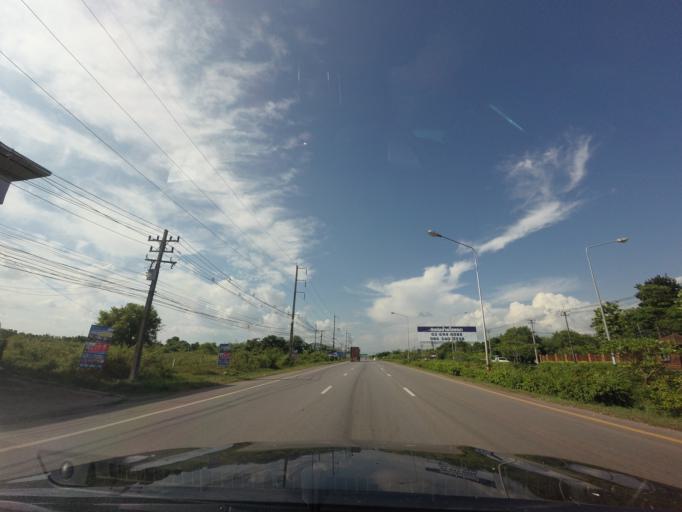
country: TH
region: Nong Khai
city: Nong Khai
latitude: 17.8062
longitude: 102.7604
